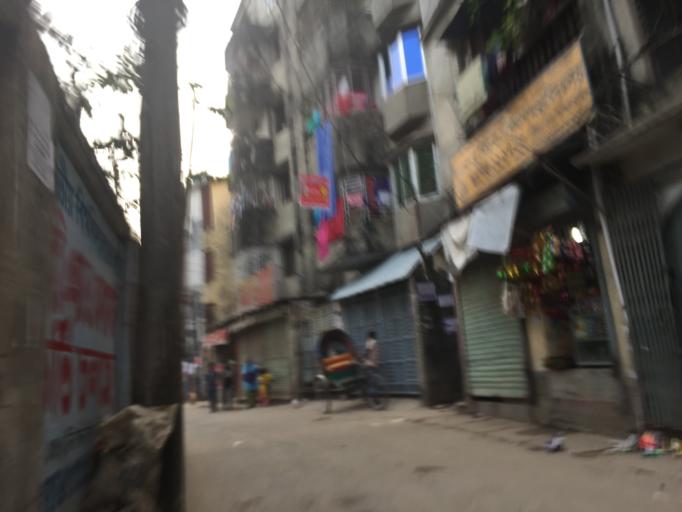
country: BD
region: Dhaka
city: Azimpur
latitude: 23.7280
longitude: 90.3813
